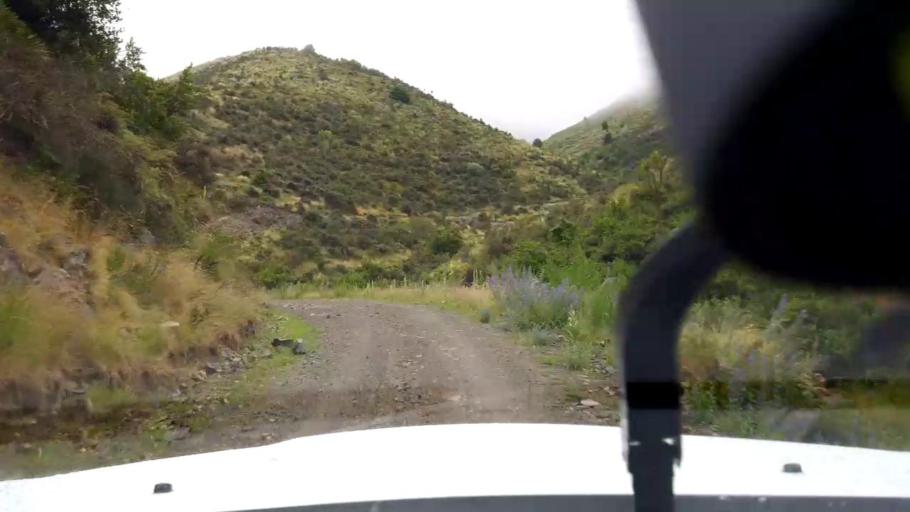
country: NZ
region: Canterbury
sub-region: Timaru District
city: Pleasant Point
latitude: -44.0336
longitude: 170.9979
